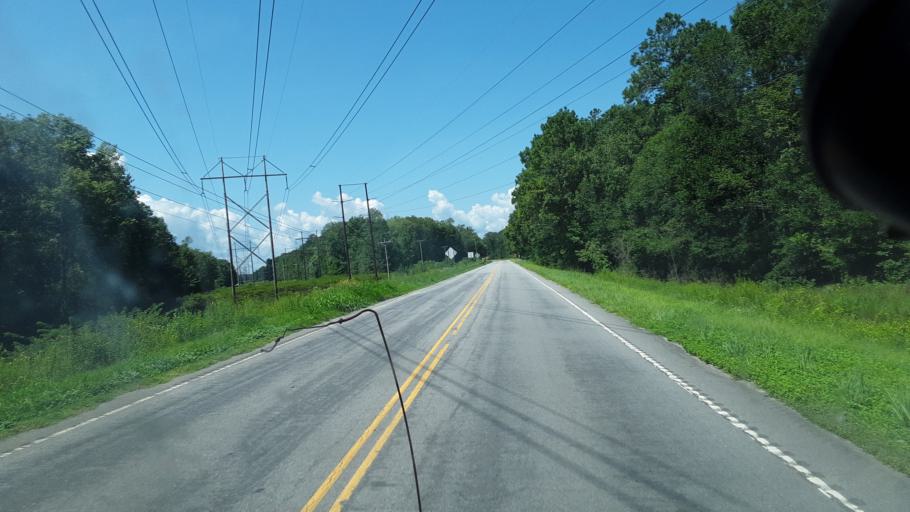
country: US
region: South Carolina
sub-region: Berkeley County
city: Bonneau Beach
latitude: 33.2690
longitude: -79.9036
